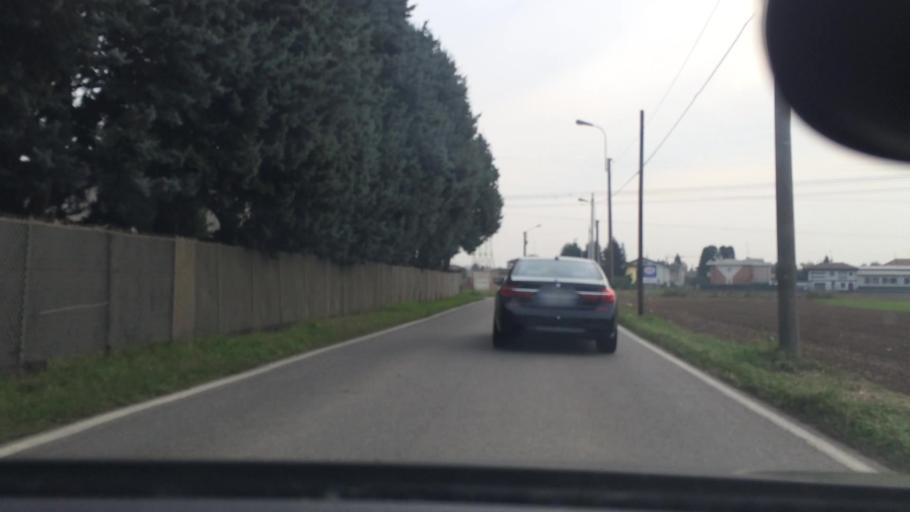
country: IT
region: Lombardy
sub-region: Provincia di Monza e Brianza
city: Misinto
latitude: 45.6543
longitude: 9.0822
